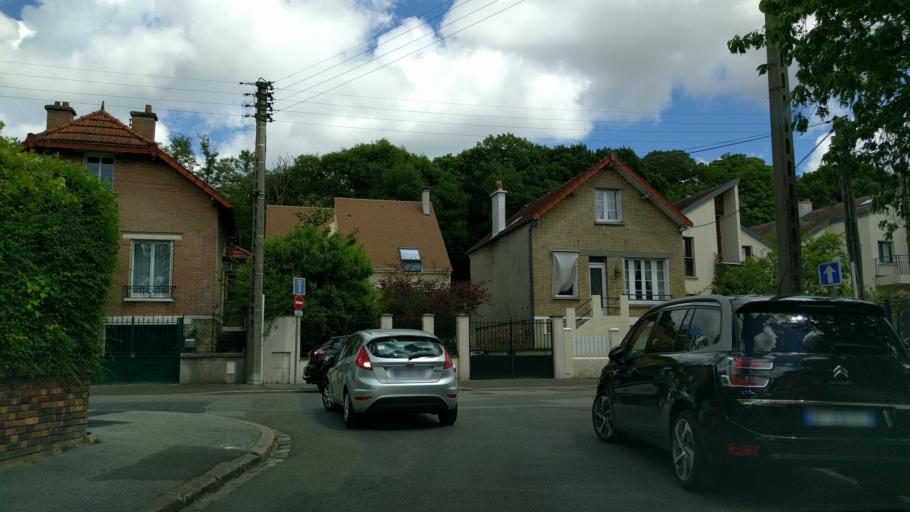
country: FR
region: Ile-de-France
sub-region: Departement des Yvelines
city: Le Chesnay
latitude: 48.8260
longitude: 2.1408
